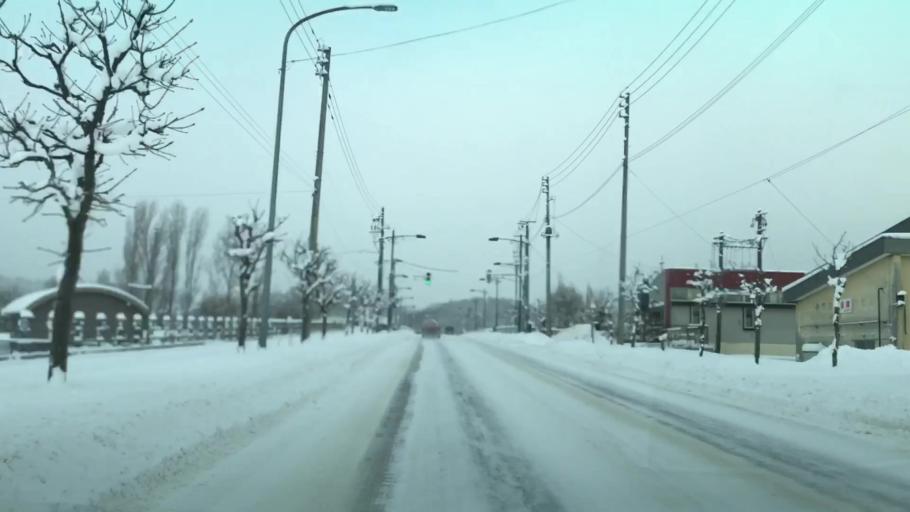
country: JP
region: Hokkaido
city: Yoichi
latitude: 43.1898
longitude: 140.7890
